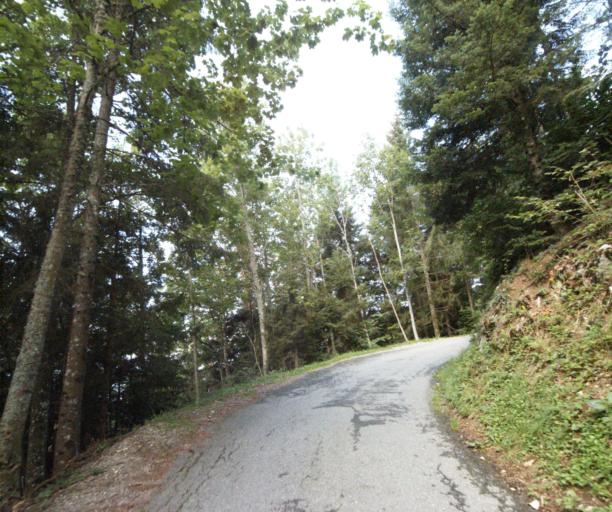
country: CH
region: Vaud
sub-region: Riviera-Pays-d'Enhaut District
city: Caux
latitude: 46.4127
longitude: 6.9450
